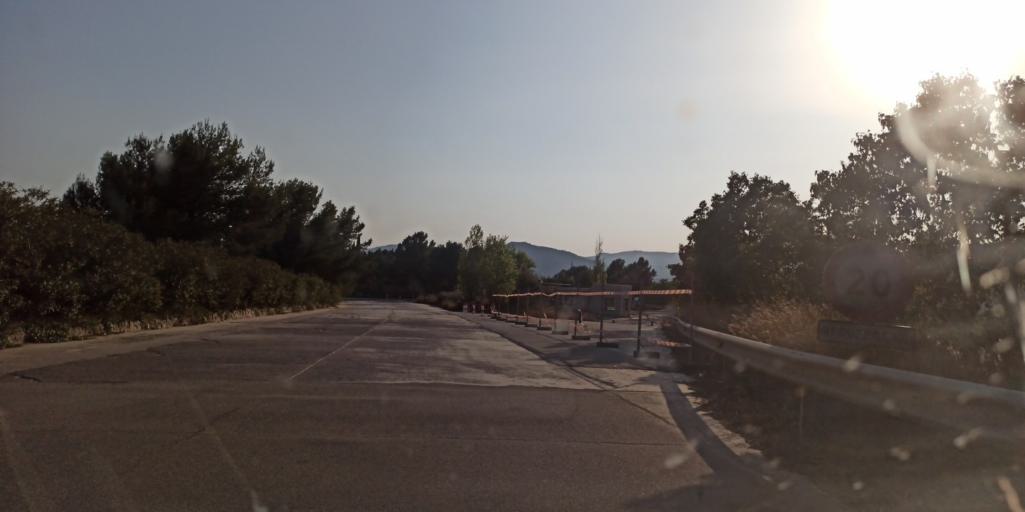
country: ES
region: Catalonia
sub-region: Provincia de Barcelona
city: Sant Feliu de Llobregat
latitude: 41.3997
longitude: 2.0553
